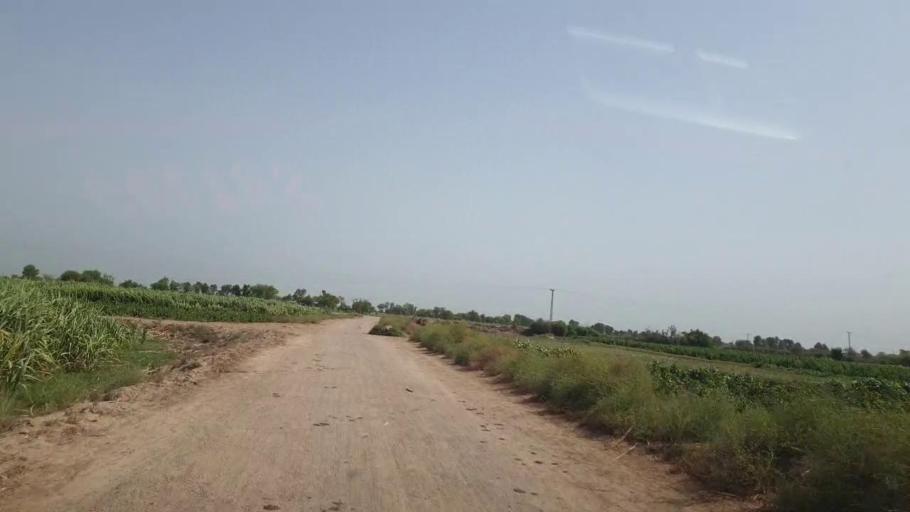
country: PK
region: Sindh
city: Daur
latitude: 26.3180
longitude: 68.2154
